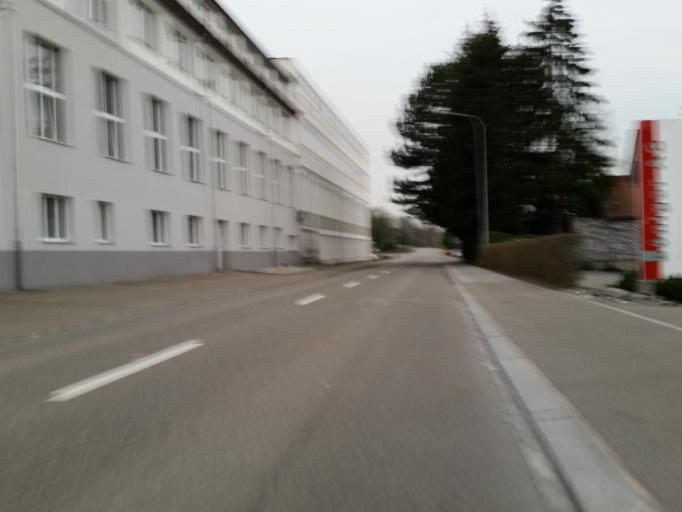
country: CH
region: Saint Gallen
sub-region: Wahlkreis Rorschach
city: Rorschach
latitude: 47.4784
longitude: 9.5192
